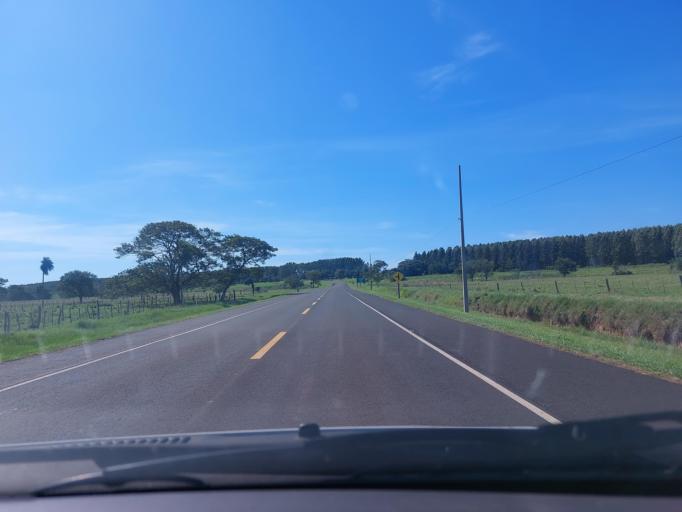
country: PY
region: San Pedro
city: Itacurubi del Rosario
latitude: -24.6036
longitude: -56.7679
